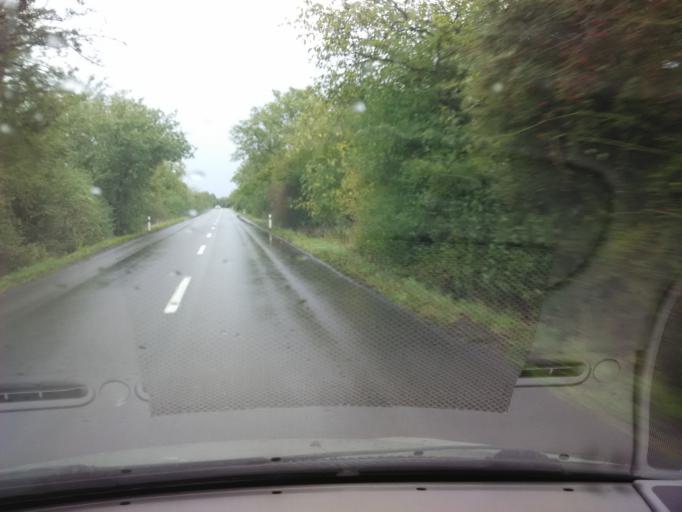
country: SK
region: Nitriansky
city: Tlmace
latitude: 48.3435
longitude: 18.4851
